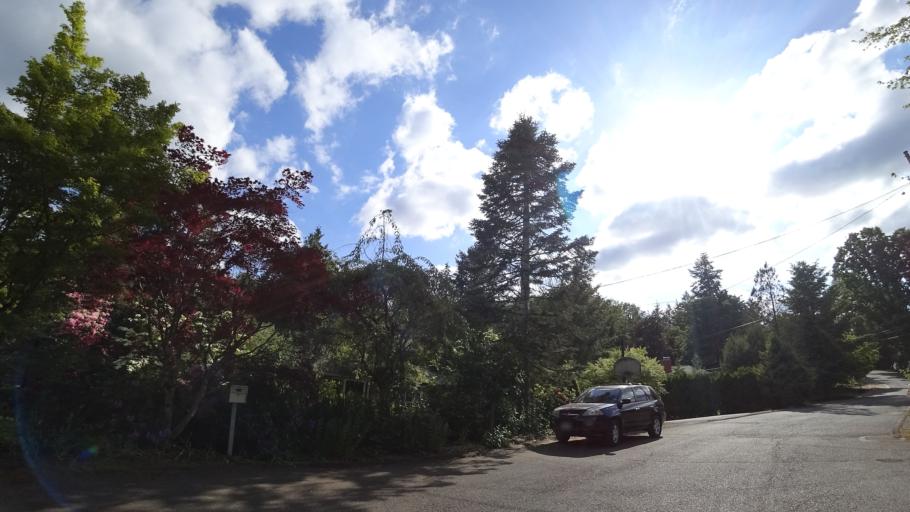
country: US
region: Oregon
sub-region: Washington County
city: Garden Home-Whitford
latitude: 45.4812
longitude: -122.7133
